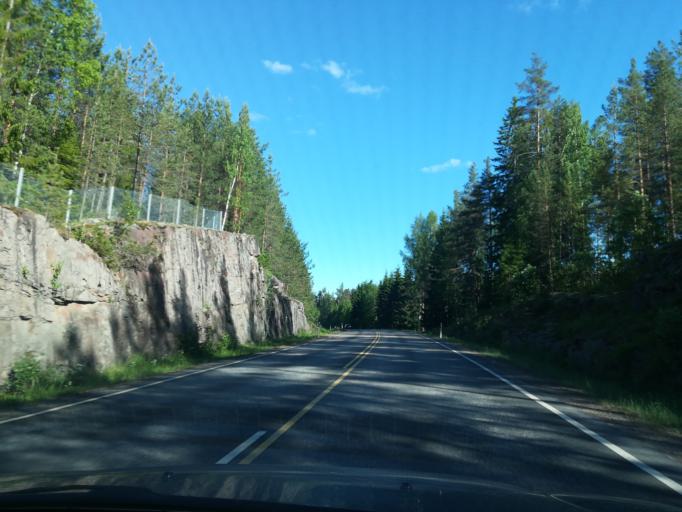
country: FI
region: South Karelia
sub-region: Imatra
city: Ruokolahti
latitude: 61.3600
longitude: 28.7037
